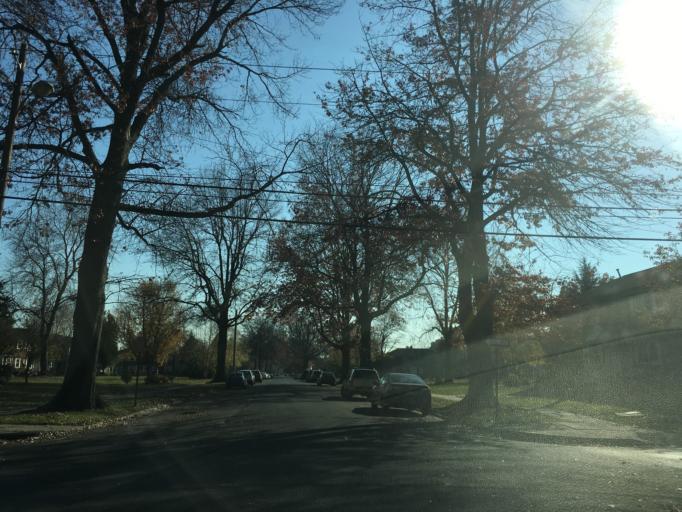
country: US
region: Pennsylvania
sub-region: Cumberland County
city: West Fairview
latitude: 40.2885
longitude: -76.9017
